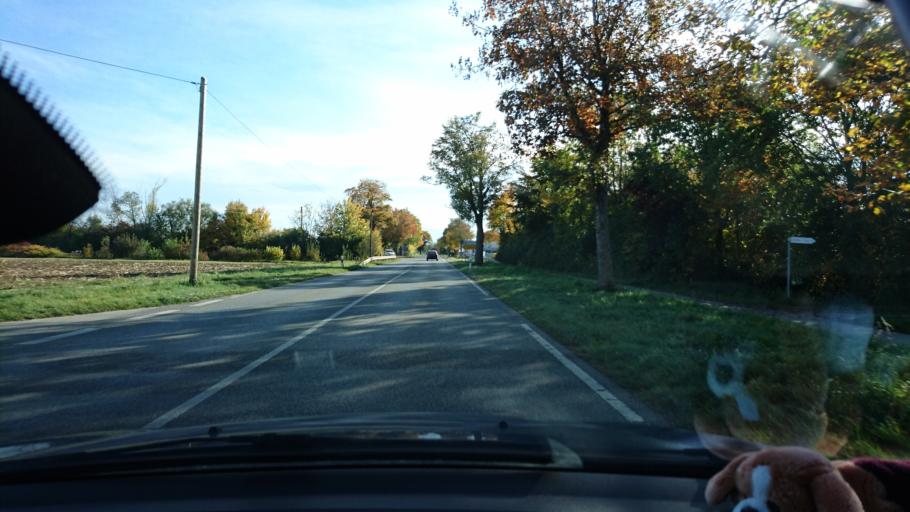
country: DE
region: Bavaria
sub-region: Upper Bavaria
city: Sauerlach
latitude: 47.9493
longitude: 11.6503
